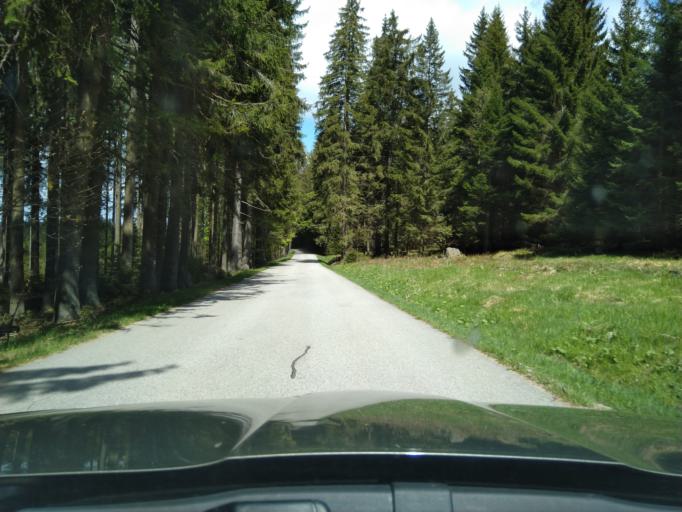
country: CZ
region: Jihocesky
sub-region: Okres Prachatice
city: Borova Lada
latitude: 49.0087
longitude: 13.7100
